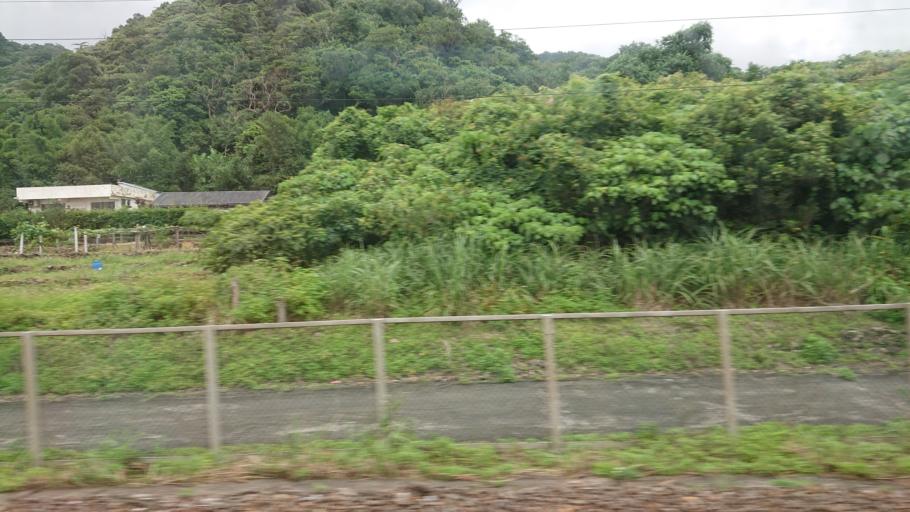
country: TW
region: Taiwan
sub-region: Keelung
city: Keelung
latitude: 24.9512
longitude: 121.9092
